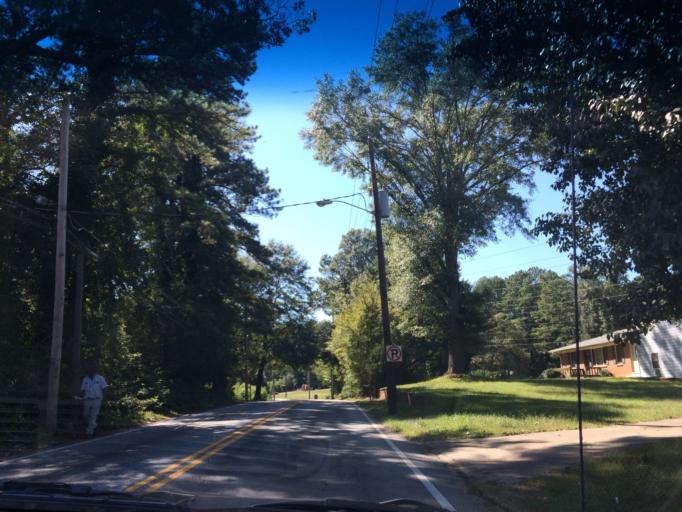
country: US
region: Georgia
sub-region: Fulton County
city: College Park
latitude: 33.6595
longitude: -84.4786
